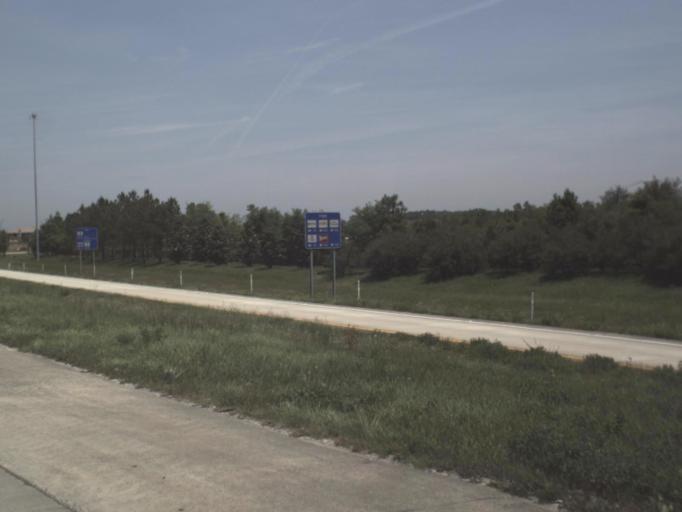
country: US
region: Florida
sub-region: Saint Johns County
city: Ponte Vedra Beach
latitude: 30.2129
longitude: -81.5137
